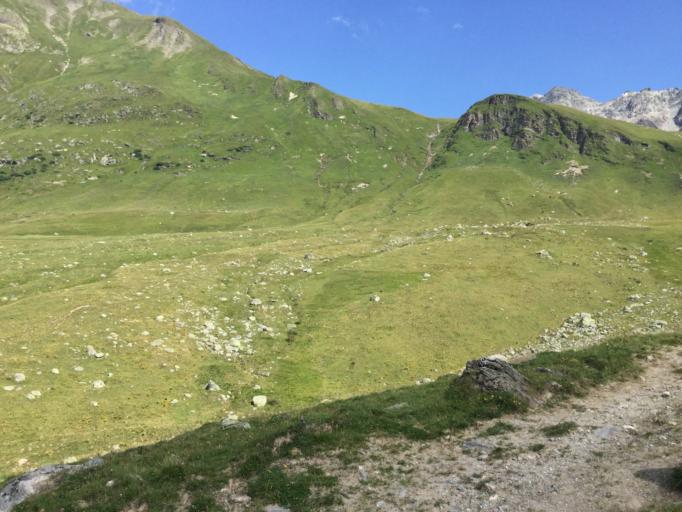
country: CH
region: Grisons
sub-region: Maloja District
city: Silvaplana
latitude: 46.4424
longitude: 9.6584
